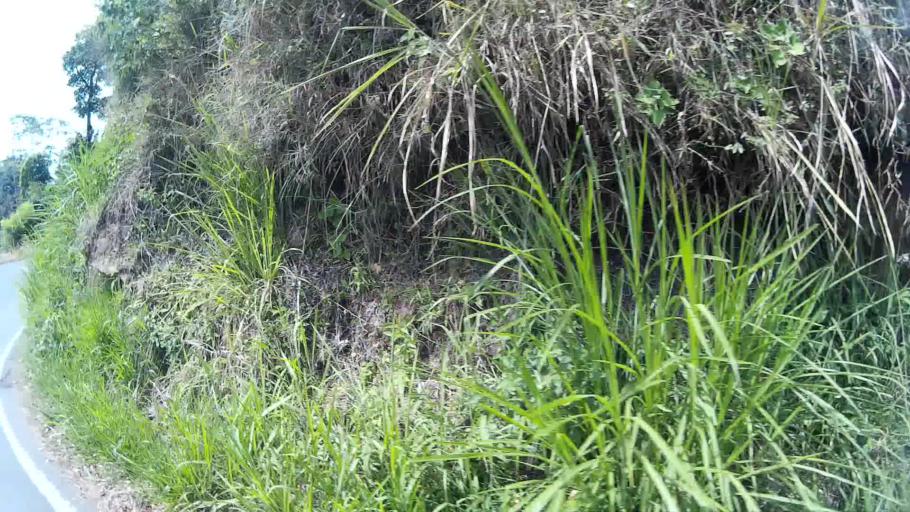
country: CO
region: Risaralda
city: Marsella
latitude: 4.9021
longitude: -75.7409
